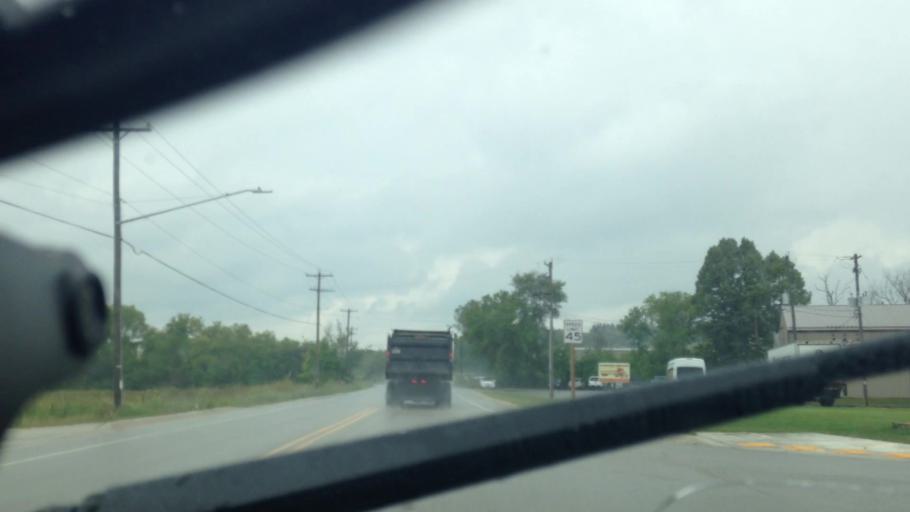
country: US
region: Wisconsin
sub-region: Washington County
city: Richfield
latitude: 43.2338
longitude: -88.1853
